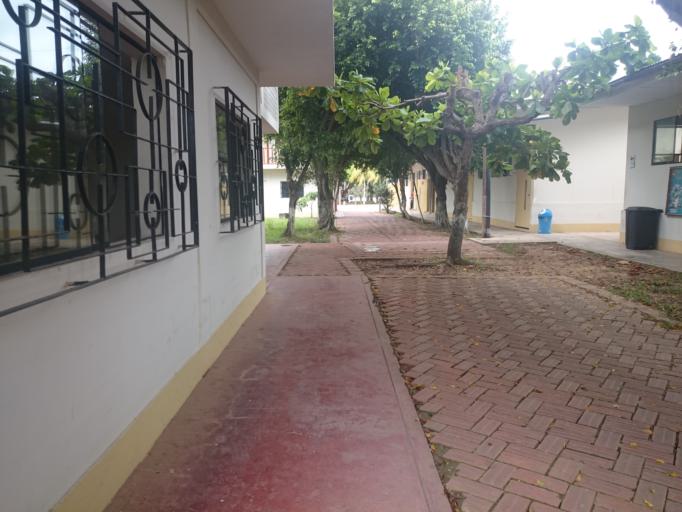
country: PE
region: Ucayali
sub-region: Provincia de Coronel Portillo
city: Puerto Callao
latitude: -8.3705
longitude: -74.5658
